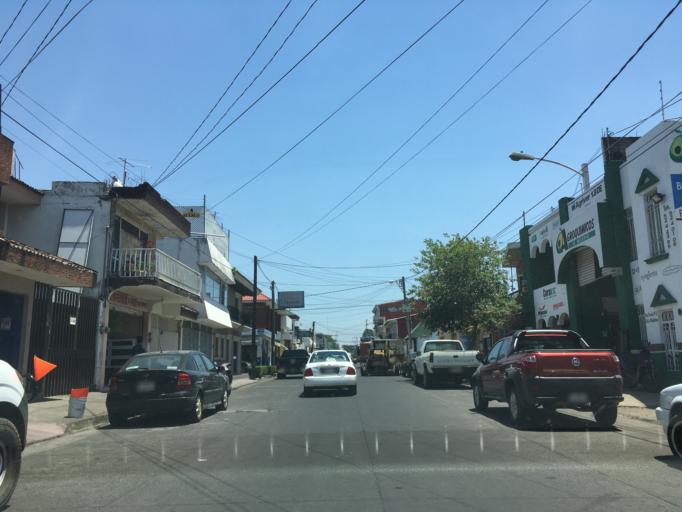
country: MX
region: Michoacan
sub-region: Uruapan
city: Uruapan
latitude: 19.4104
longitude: -102.0575
